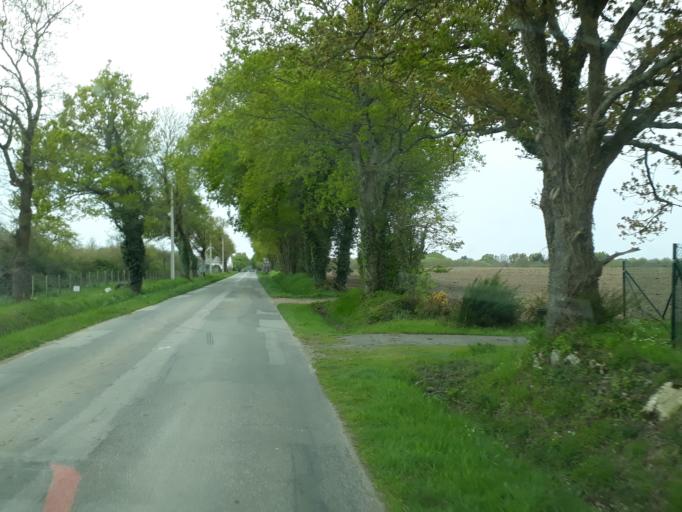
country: FR
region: Brittany
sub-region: Departement du Morbihan
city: Theix
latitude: 47.6226
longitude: -2.6771
